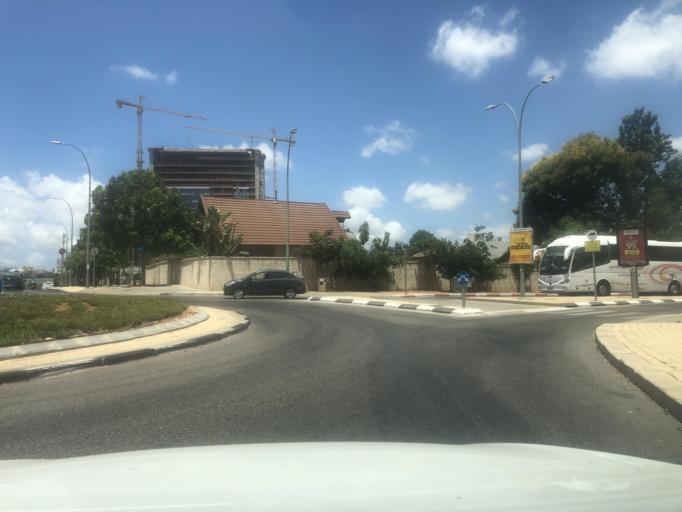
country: IL
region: Central District
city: Kfar Saba
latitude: 32.1660
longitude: 34.9018
